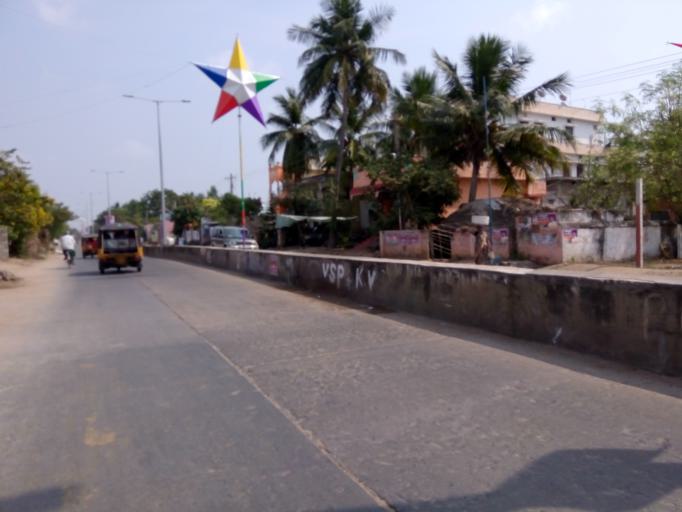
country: IN
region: Andhra Pradesh
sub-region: Prakasam
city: Chirala
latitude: 15.8373
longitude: 80.3659
